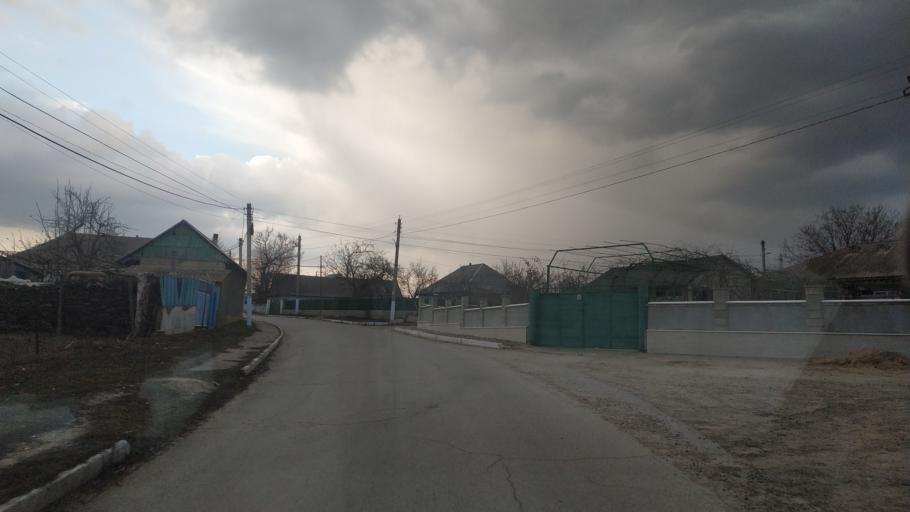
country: MD
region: Telenesti
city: Grigoriopol
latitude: 47.0263
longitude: 29.3553
